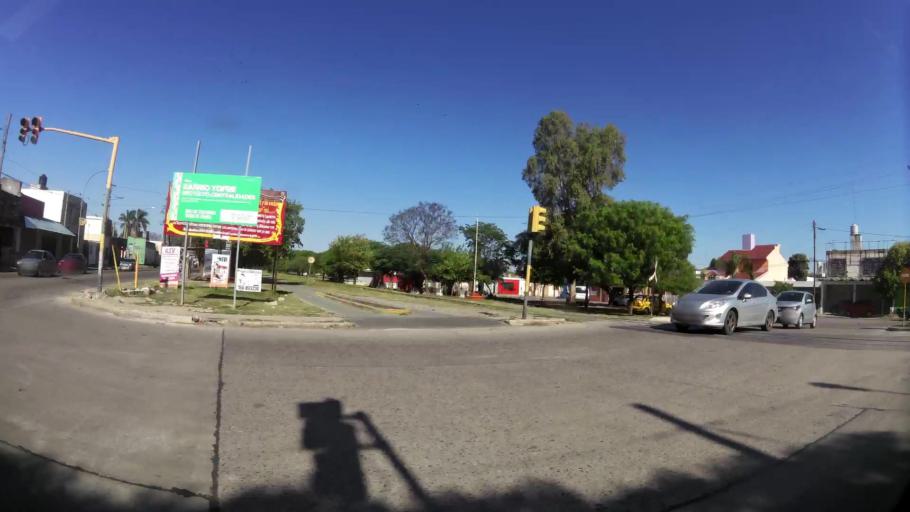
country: AR
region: Cordoba
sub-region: Departamento de Capital
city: Cordoba
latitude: -31.3891
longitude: -64.1342
